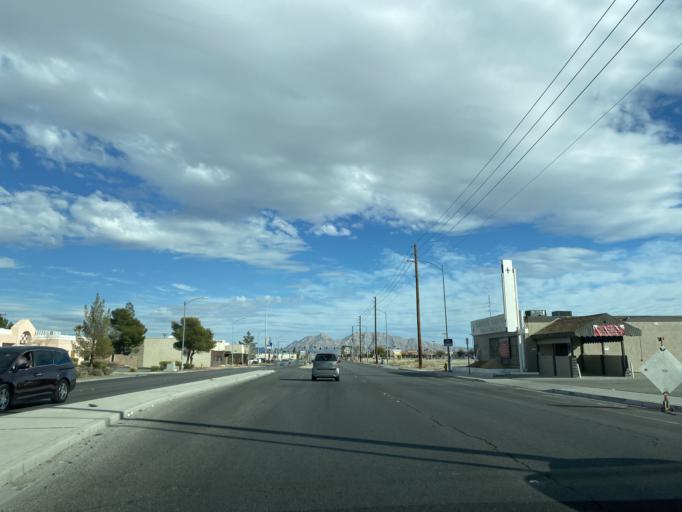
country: US
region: Nevada
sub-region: Clark County
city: Las Vegas
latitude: 36.1884
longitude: -115.1591
